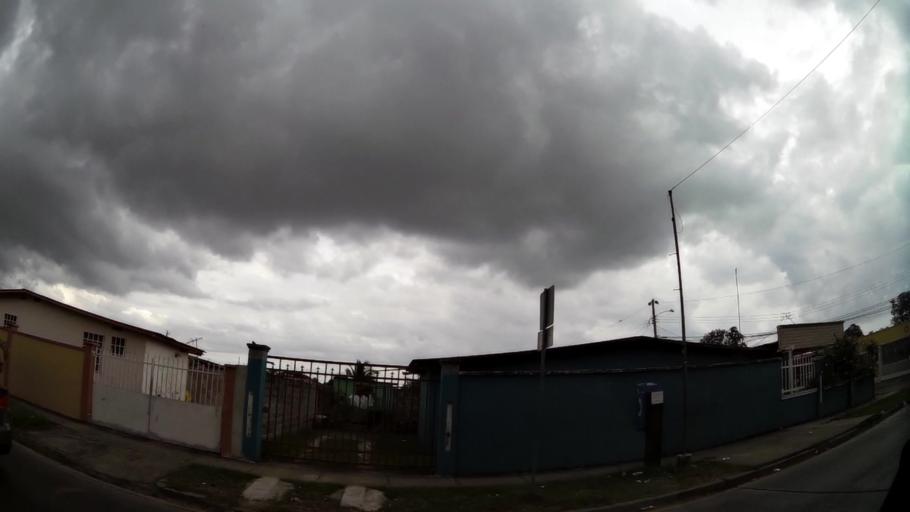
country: PA
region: Panama
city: Tocumen
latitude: 9.0512
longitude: -79.4091
